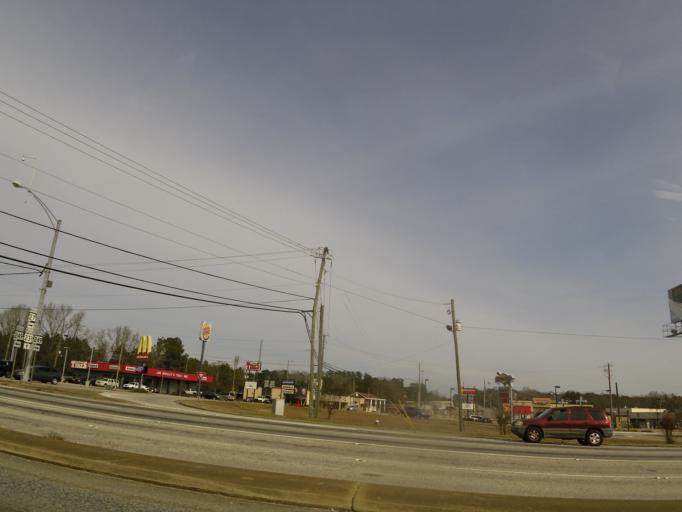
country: US
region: Alabama
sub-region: Dale County
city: Ozark
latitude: 31.4477
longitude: -85.6578
